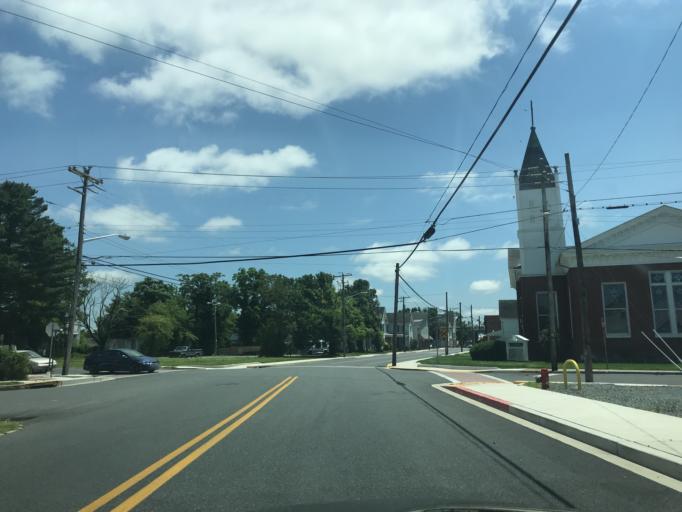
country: US
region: Maryland
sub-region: Dorchester County
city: Hurlock
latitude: 38.6353
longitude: -75.8648
